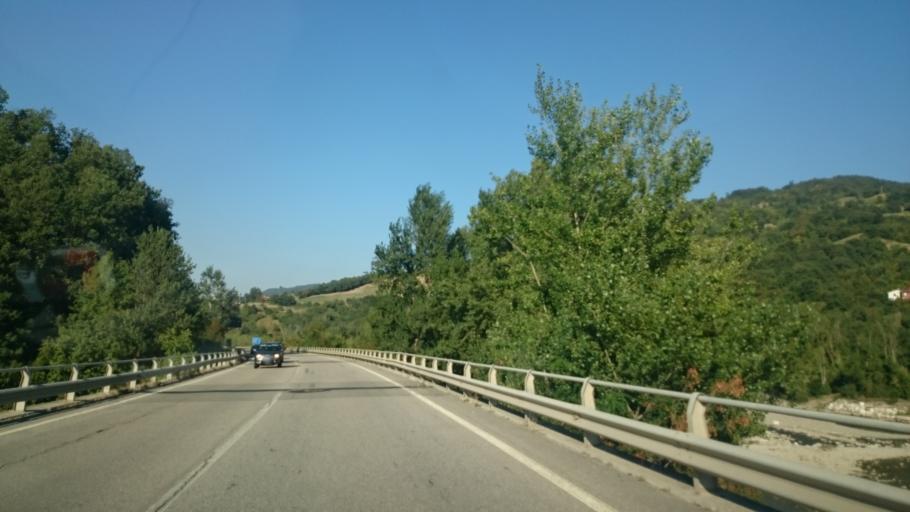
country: IT
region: Emilia-Romagna
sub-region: Provincia di Modena
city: Montefiorino
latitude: 44.4090
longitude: 10.6248
